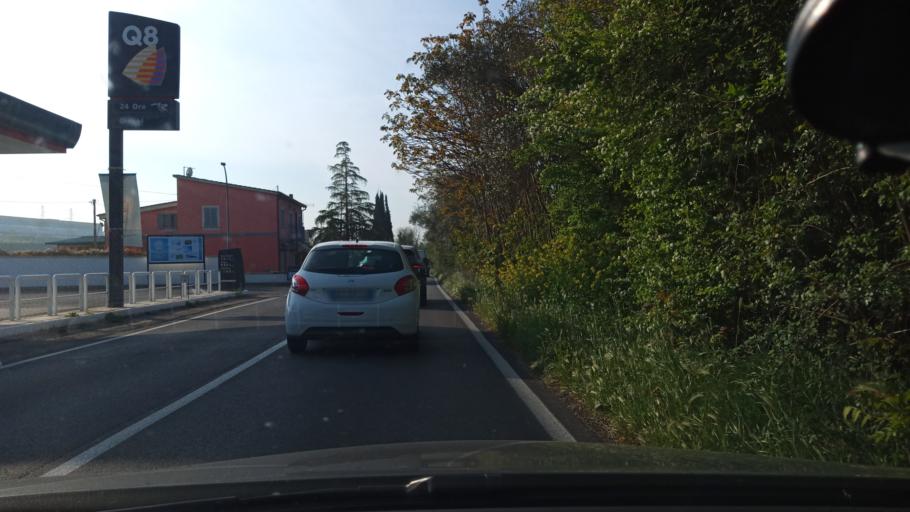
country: IT
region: Latium
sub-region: Citta metropolitana di Roma Capitale
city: Fiano Romano
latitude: 42.1700
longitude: 12.6367
